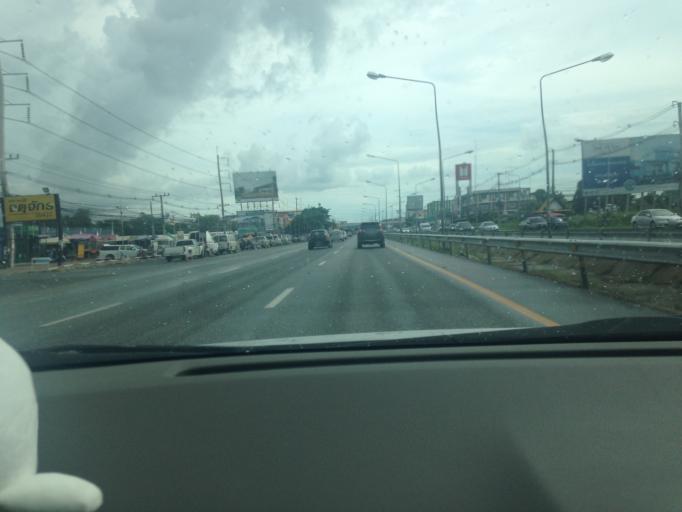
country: TH
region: Chon Buri
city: Chon Buri
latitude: 13.3015
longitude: 100.9491
